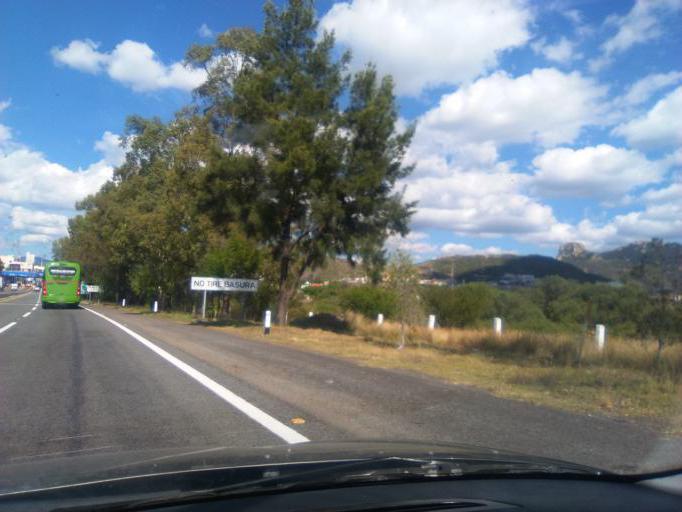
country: MX
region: Guanajuato
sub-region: Guanajuato
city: San Jose de Cervera
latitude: 20.9794
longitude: -101.2920
